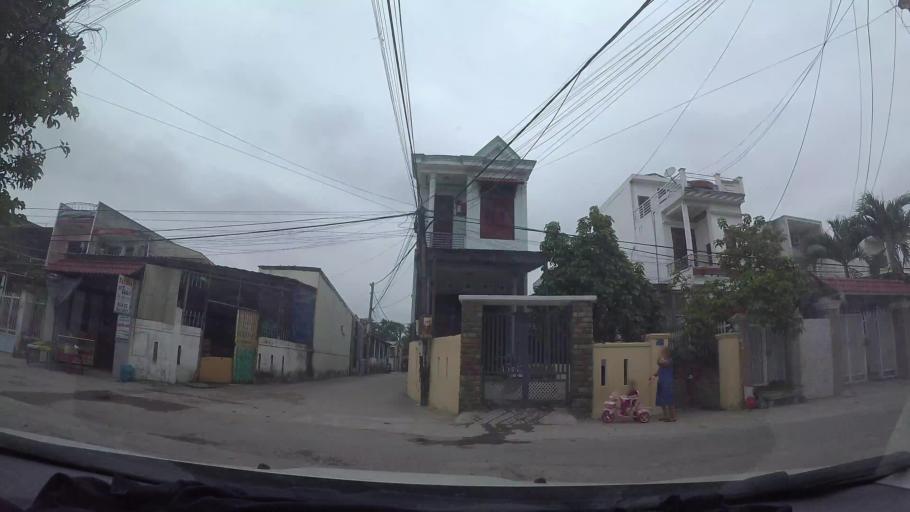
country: VN
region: Da Nang
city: Lien Chieu
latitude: 16.0863
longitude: 108.1427
